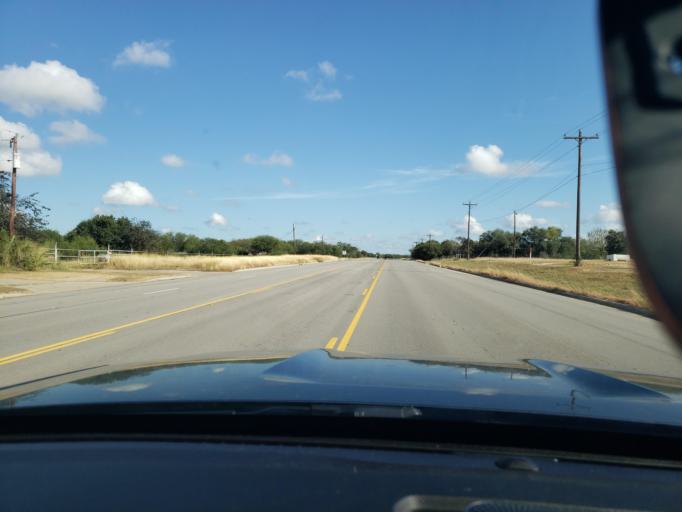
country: US
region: Texas
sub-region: Bee County
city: Beeville
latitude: 28.4351
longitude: -97.7134
